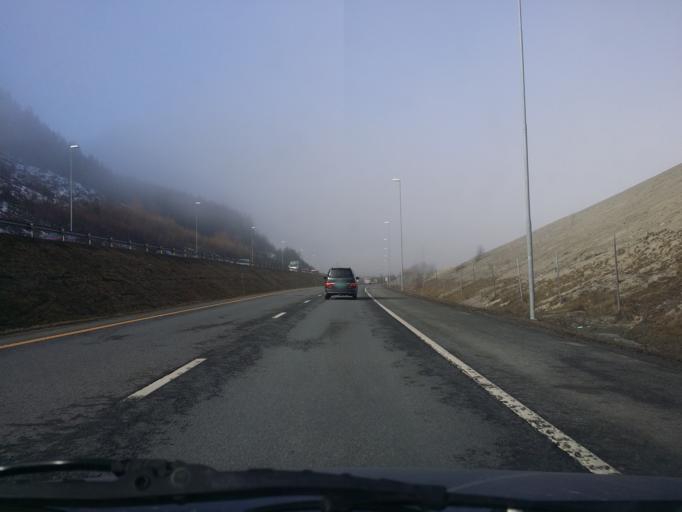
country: NO
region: Buskerud
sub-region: Nedre Eiker
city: Mjondalen
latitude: 59.7463
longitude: 10.0602
